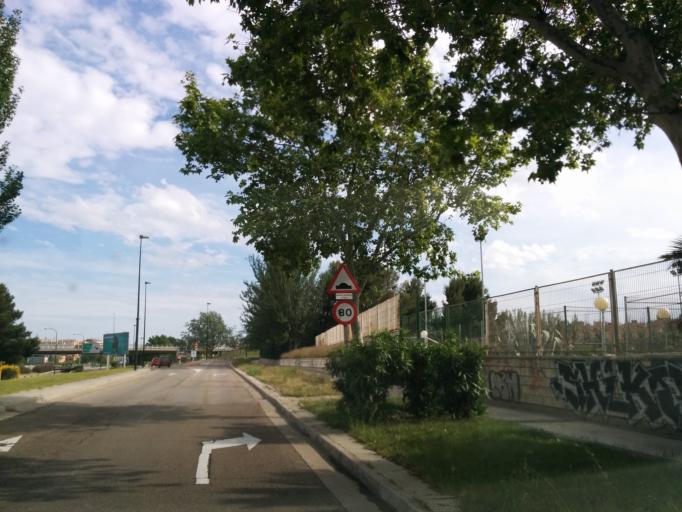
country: ES
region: Aragon
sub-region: Provincia de Zaragoza
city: Zaragoza
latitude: 41.6751
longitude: -0.8814
